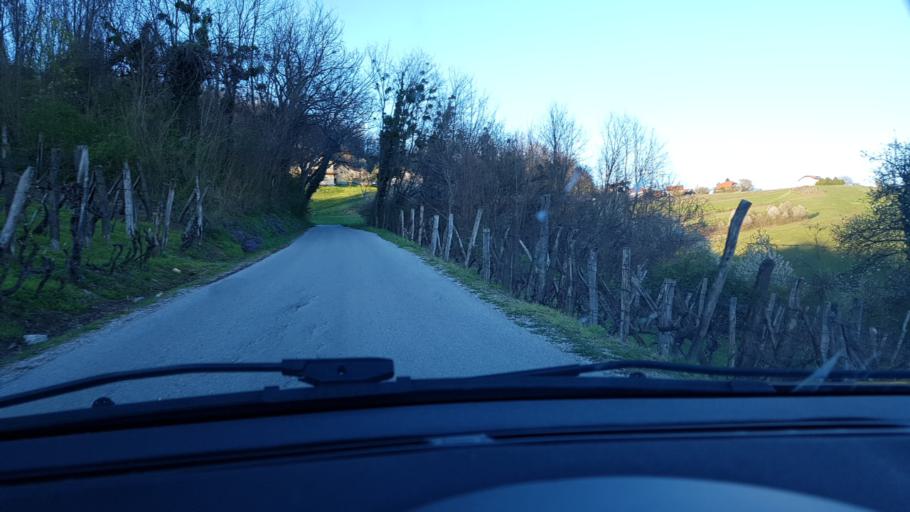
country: HR
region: Krapinsko-Zagorska
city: Pregrada
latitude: 46.1652
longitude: 15.7026
